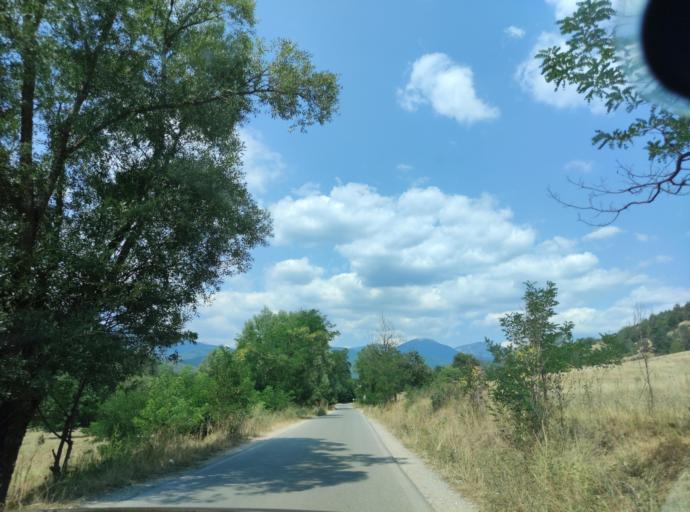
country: BG
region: Blagoevgrad
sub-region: Obshtina Belitsa
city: Belitsa
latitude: 41.9720
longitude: 23.5555
